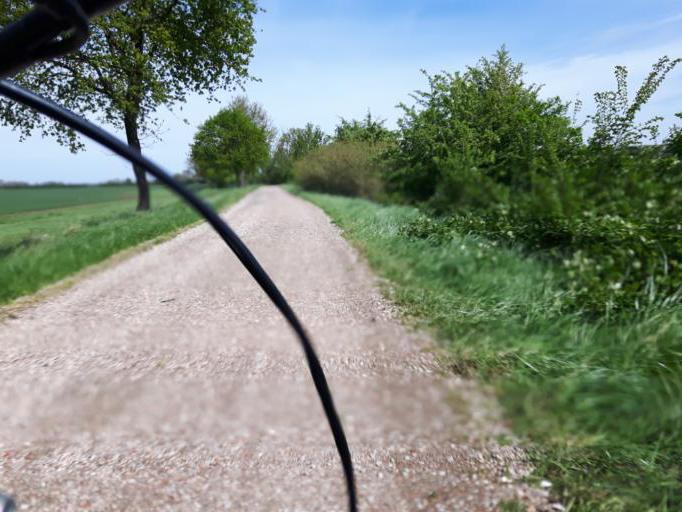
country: NL
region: Zeeland
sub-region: Gemeente Goes
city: Goes
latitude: 51.4434
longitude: 3.8557
